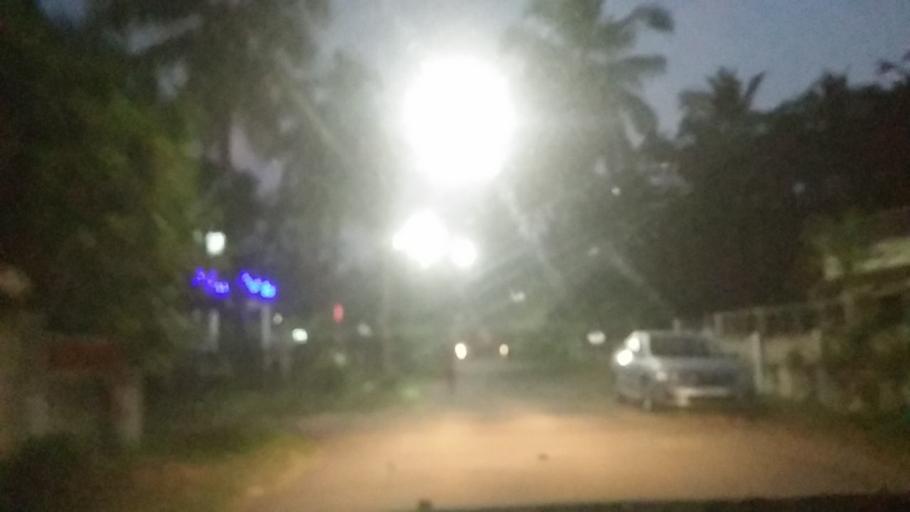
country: IN
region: Goa
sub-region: South Goa
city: Madgaon
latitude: 15.2631
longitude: 73.9648
